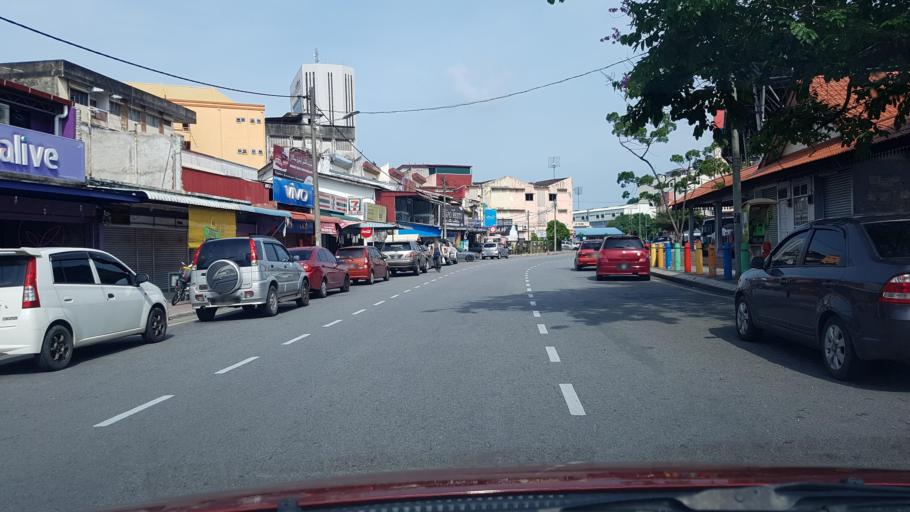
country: MY
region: Terengganu
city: Kuala Terengganu
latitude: 5.3326
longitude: 103.1373
